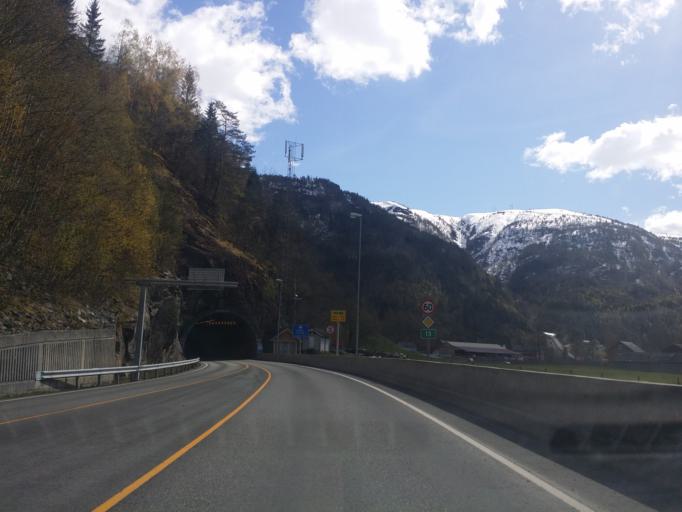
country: NO
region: Hordaland
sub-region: Granvin
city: Granvin
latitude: 60.5338
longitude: 6.7345
